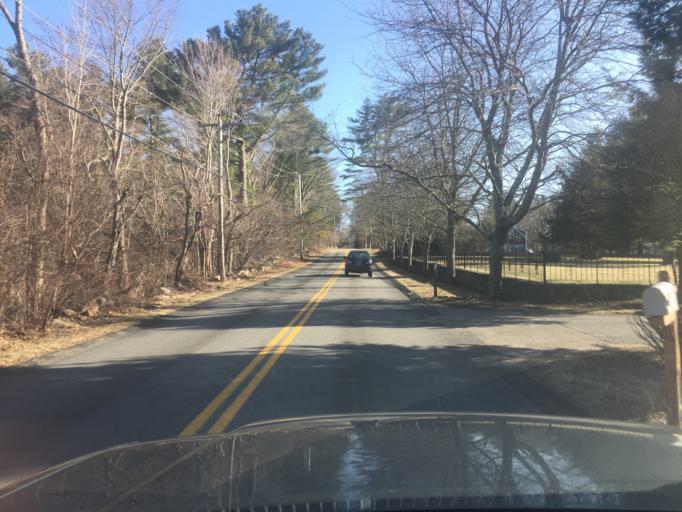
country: US
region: Massachusetts
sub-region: Norfolk County
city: Norfolk
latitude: 42.1233
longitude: -71.3599
